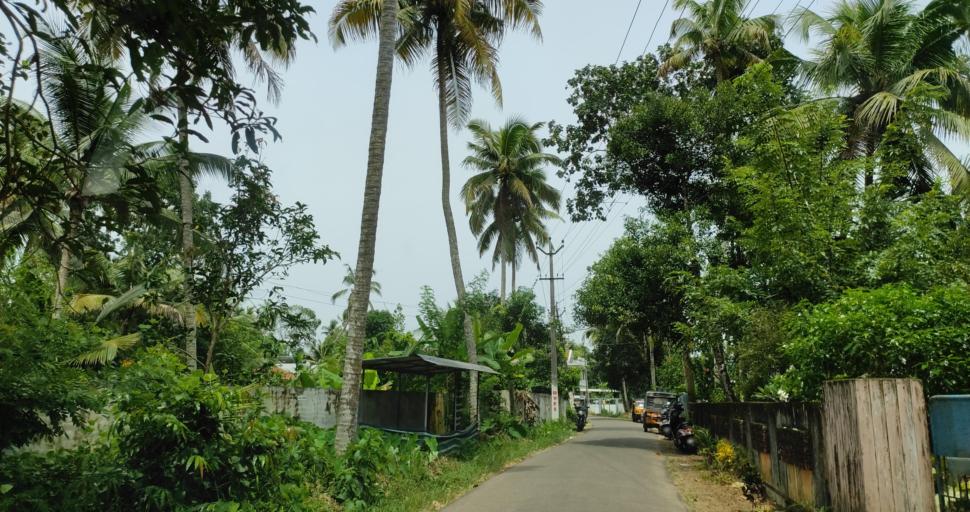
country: IN
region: Kerala
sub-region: Alappuzha
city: Shertallai
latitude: 9.6754
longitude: 76.3564
